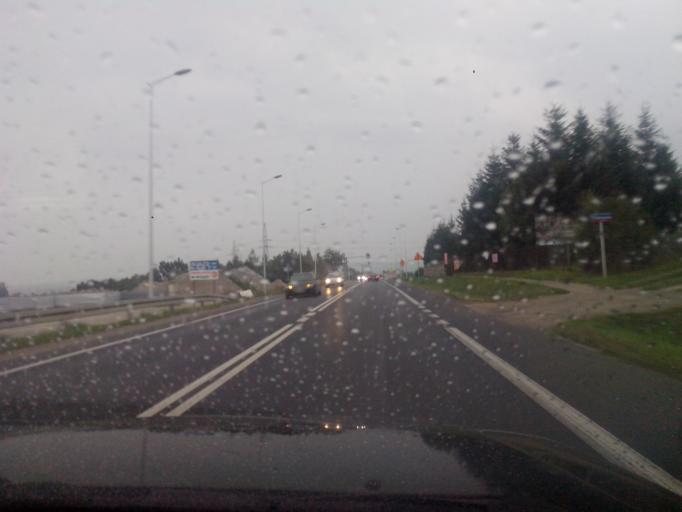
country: PL
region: Subcarpathian Voivodeship
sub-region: Powiat rzeszowski
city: Boguchwala
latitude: 49.9981
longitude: 21.9569
